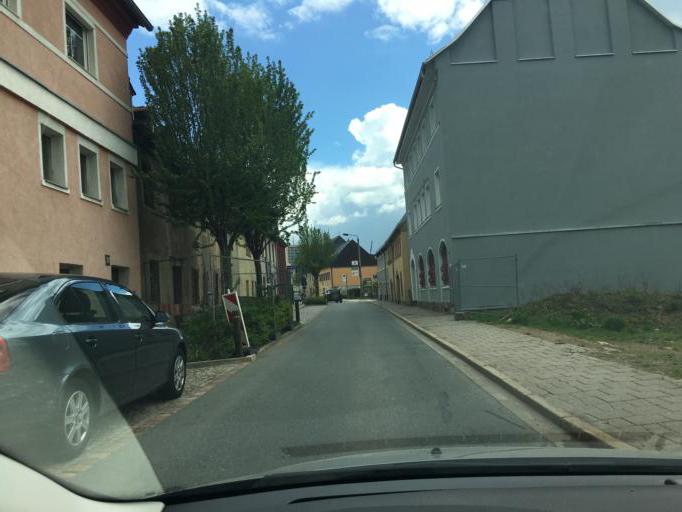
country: DE
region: Saxony
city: Hohenstein-Ernstthal
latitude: 50.8007
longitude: 12.7171
